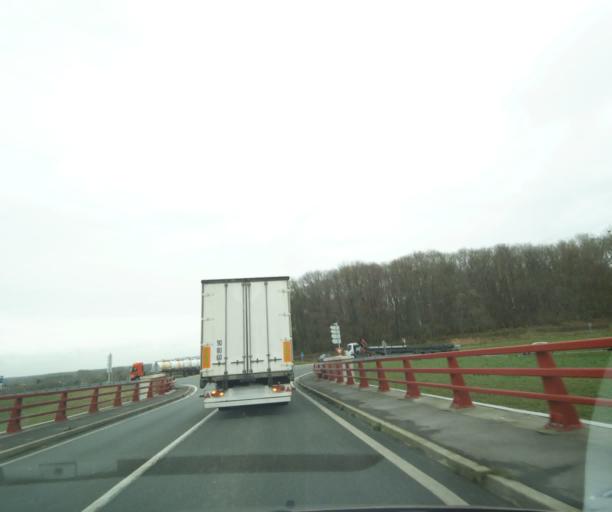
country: FR
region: Picardie
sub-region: Departement de l'Oise
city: Noyon
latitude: 49.5672
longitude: 2.9740
